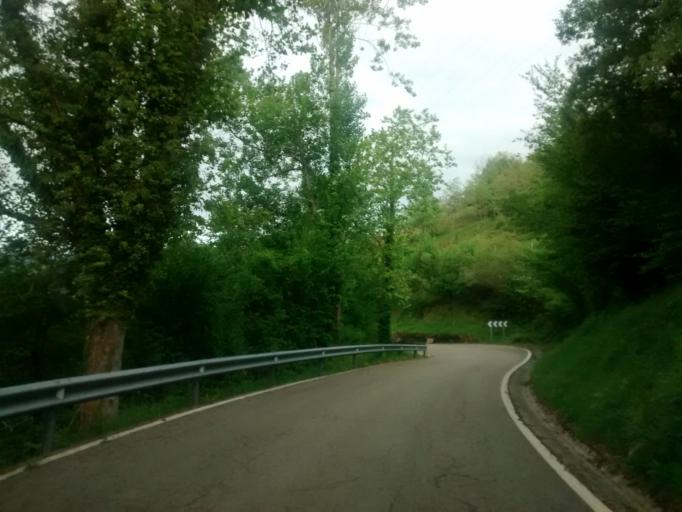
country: ES
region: Cantabria
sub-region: Provincia de Cantabria
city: San Vicente de la Barquera
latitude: 43.2538
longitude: -4.4381
